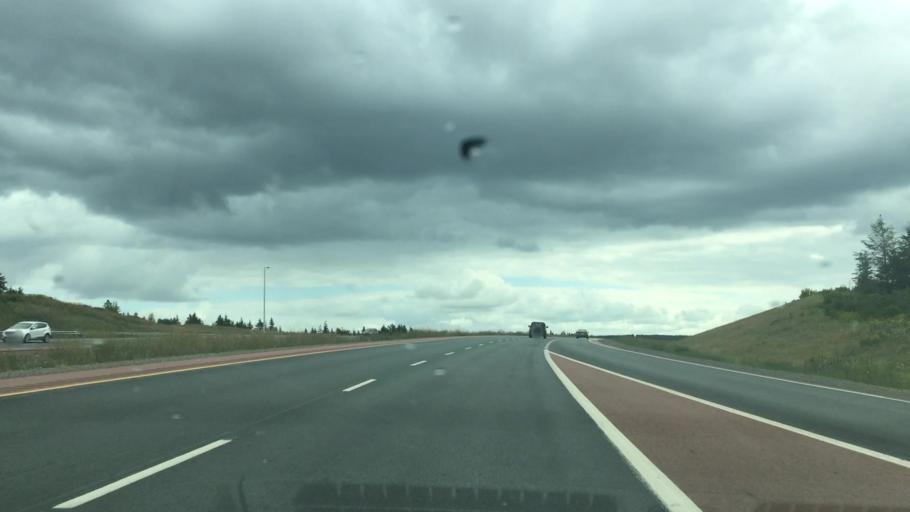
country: CA
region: Nova Scotia
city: Antigonish
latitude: 45.6091
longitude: -61.9631
